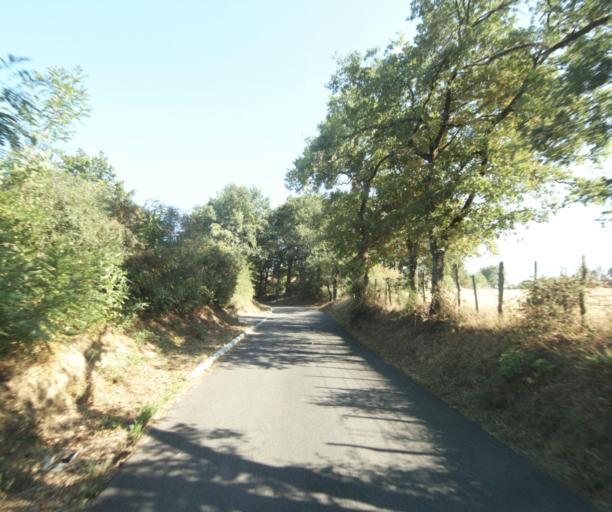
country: FR
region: Rhone-Alpes
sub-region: Departement du Rhone
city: Sainte-Consorce
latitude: 45.8013
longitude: 4.6915
